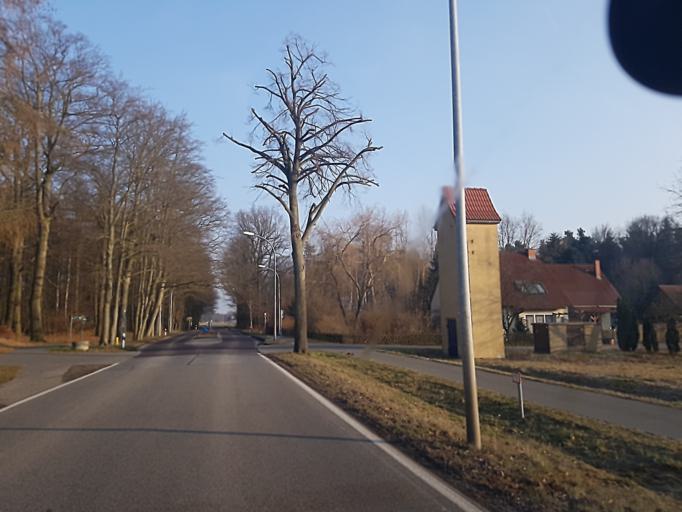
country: DE
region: Brandenburg
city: Wiesenburg
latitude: 52.1193
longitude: 12.4314
